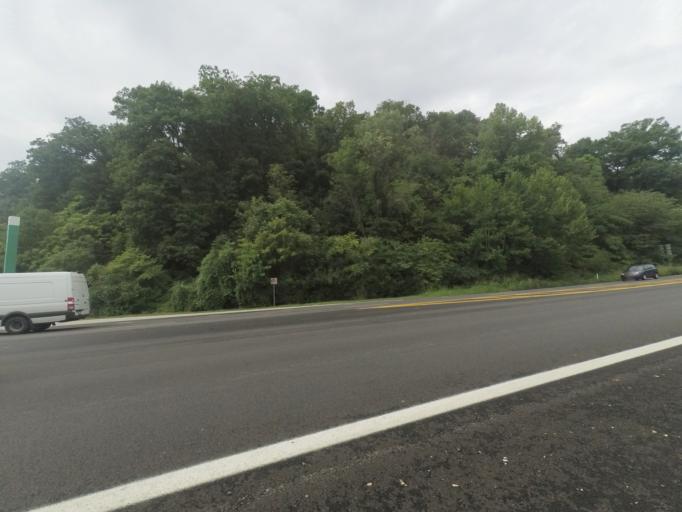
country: US
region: West Virginia
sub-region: Cabell County
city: Huntington
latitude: 38.3964
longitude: -82.4500
